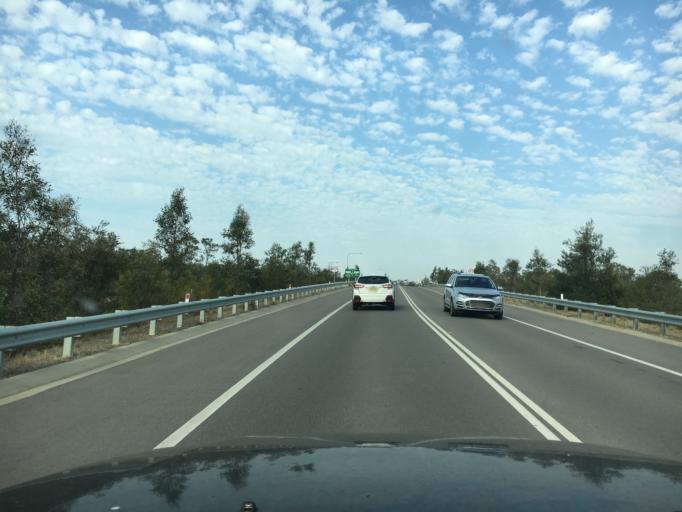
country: AU
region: New South Wales
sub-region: Cessnock
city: Branxton
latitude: -32.6658
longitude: 151.3649
